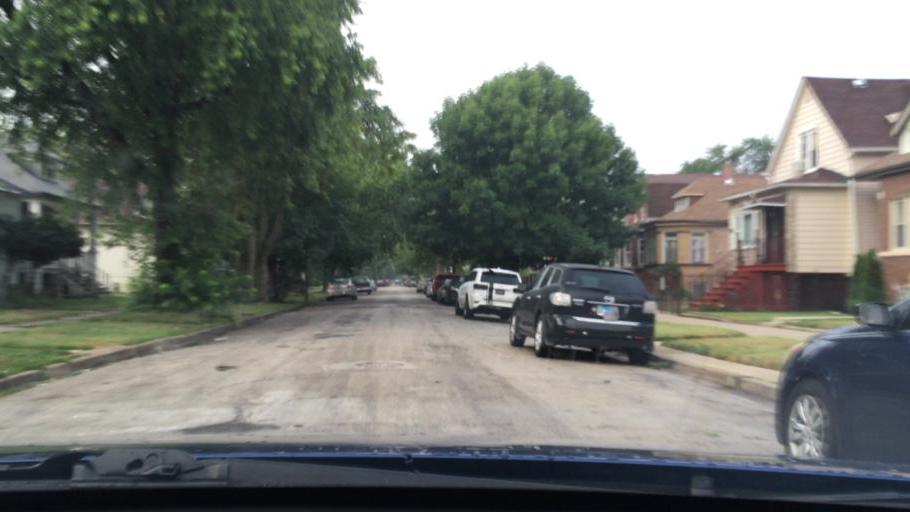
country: US
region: Illinois
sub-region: Cook County
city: Evergreen Park
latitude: 41.7430
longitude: -87.6499
